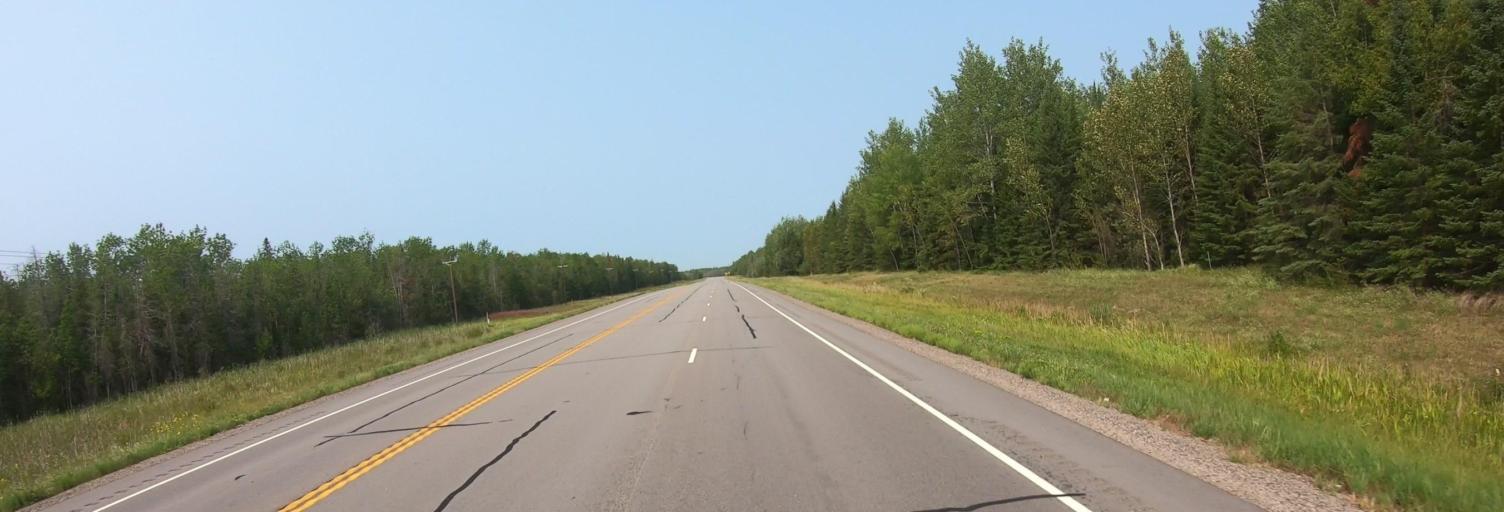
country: CA
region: Ontario
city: Fort Frances
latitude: 48.4038
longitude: -93.0292
